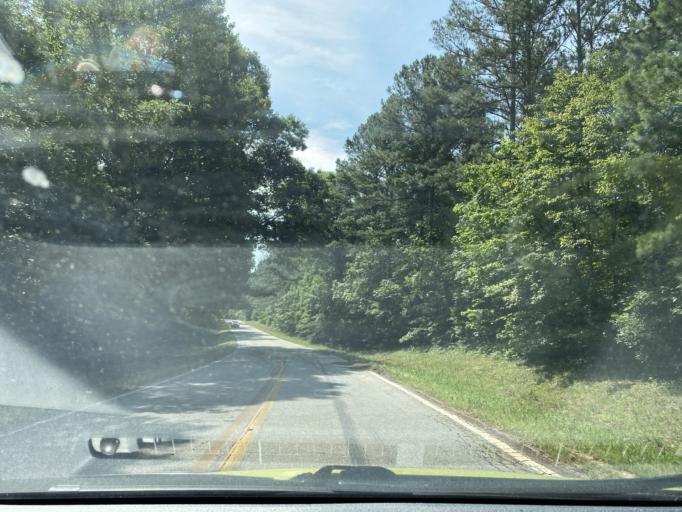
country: US
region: Georgia
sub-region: Meriwether County
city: Greenville
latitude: 33.1763
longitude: -84.6969
